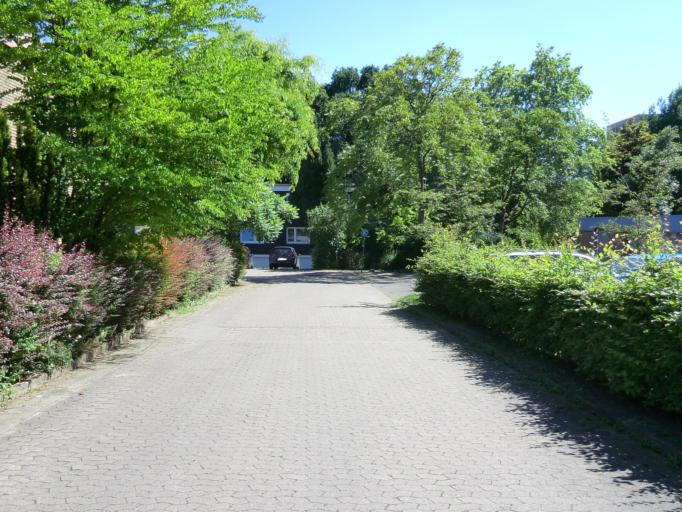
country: DE
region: North Rhine-Westphalia
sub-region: Regierungsbezirk Detmold
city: Hiddenhausen
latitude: 52.1507
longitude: 8.6387
